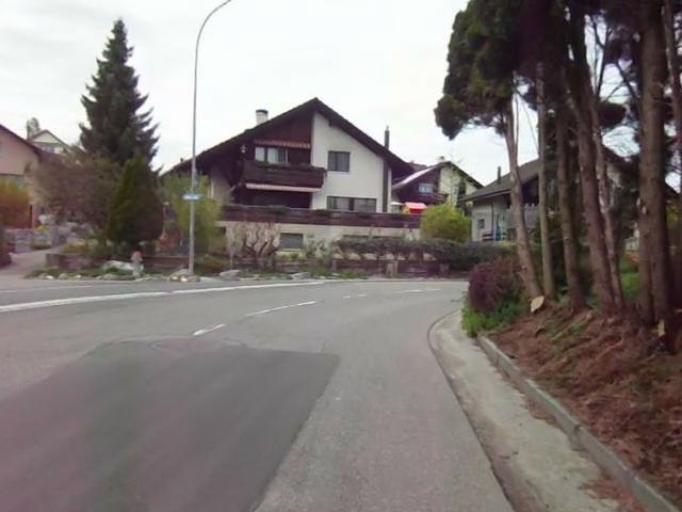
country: CH
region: Zurich
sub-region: Bezirk Hinwil
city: Rueti / Westlicher Dorfteil
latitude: 47.2555
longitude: 8.8418
